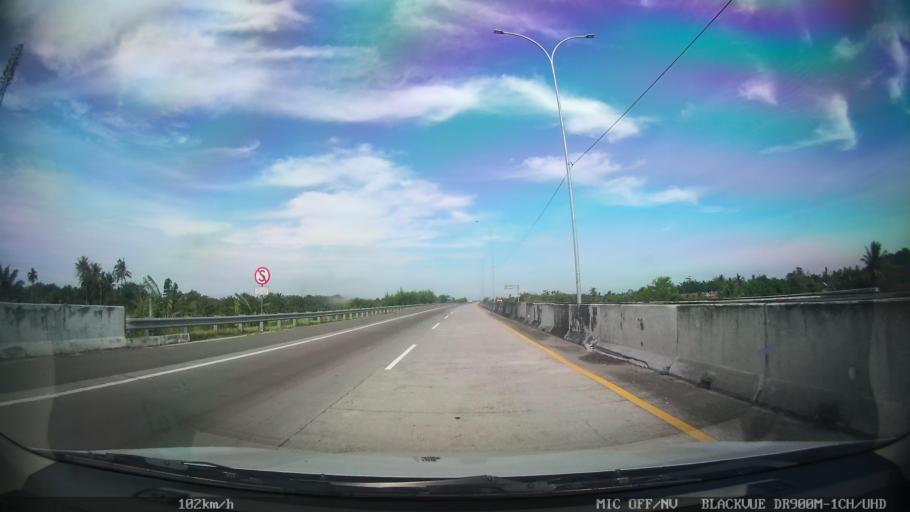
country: ID
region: North Sumatra
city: Sunggal
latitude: 3.6382
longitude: 98.5768
